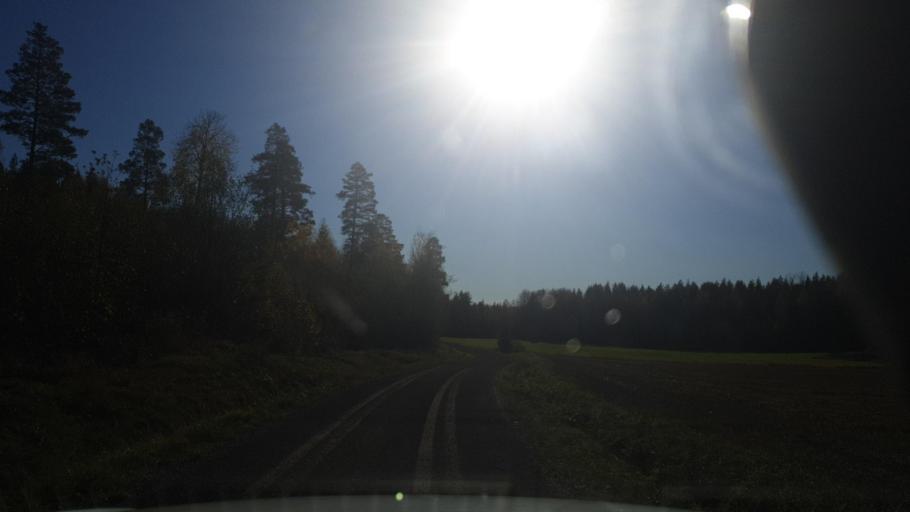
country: SE
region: Vaermland
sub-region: Grums Kommun
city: Grums
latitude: 59.5269
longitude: 12.9193
